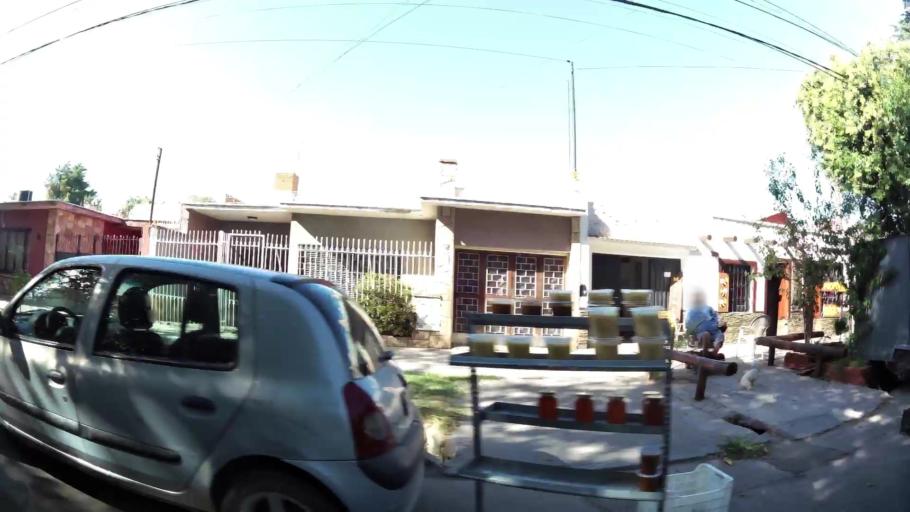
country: AR
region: Mendoza
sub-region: Departamento de Godoy Cruz
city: Godoy Cruz
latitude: -32.9251
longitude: -68.8532
